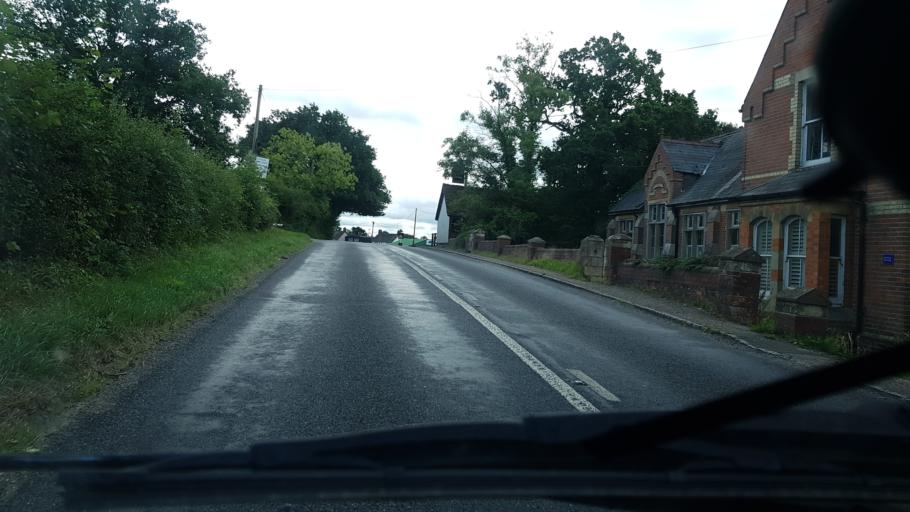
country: GB
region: England
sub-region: West Sussex
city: Rudgwick
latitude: 51.0868
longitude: -0.4630
